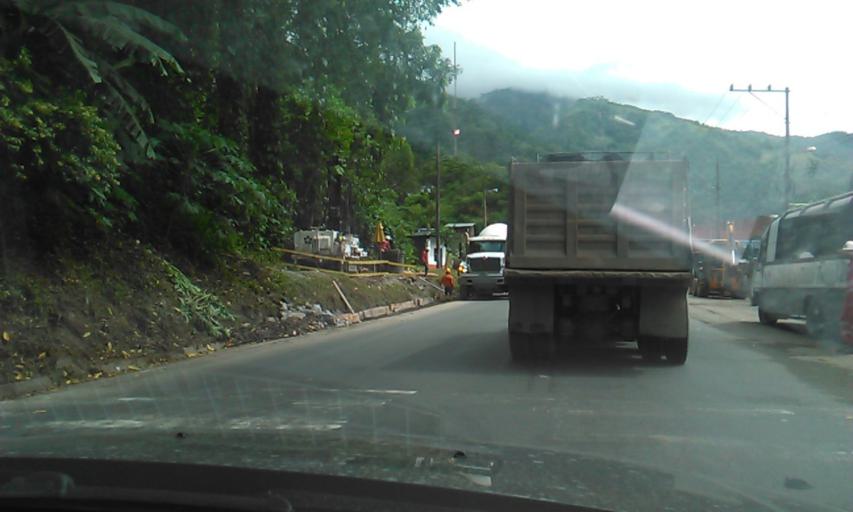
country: CO
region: Valle del Cauca
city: Dagua
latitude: 3.7833
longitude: -76.7604
